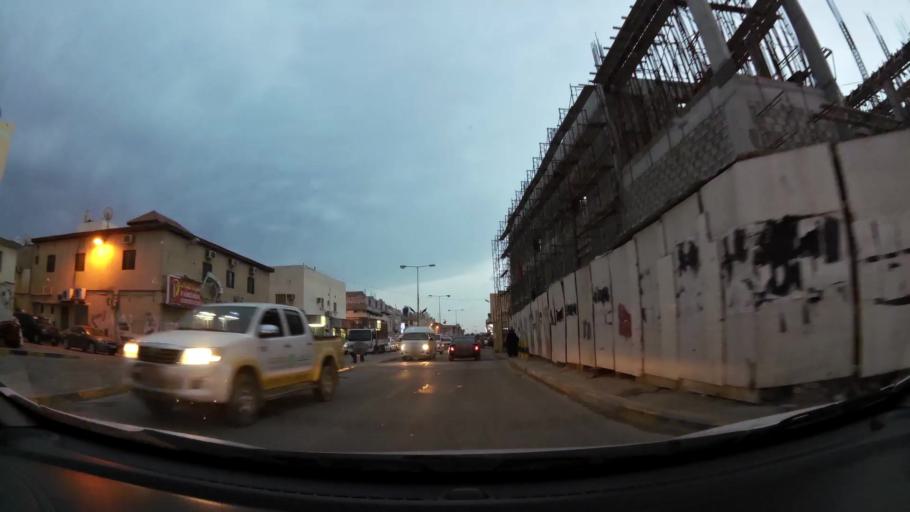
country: BH
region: Central Governorate
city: Madinat Hamad
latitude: 26.1458
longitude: 50.4979
